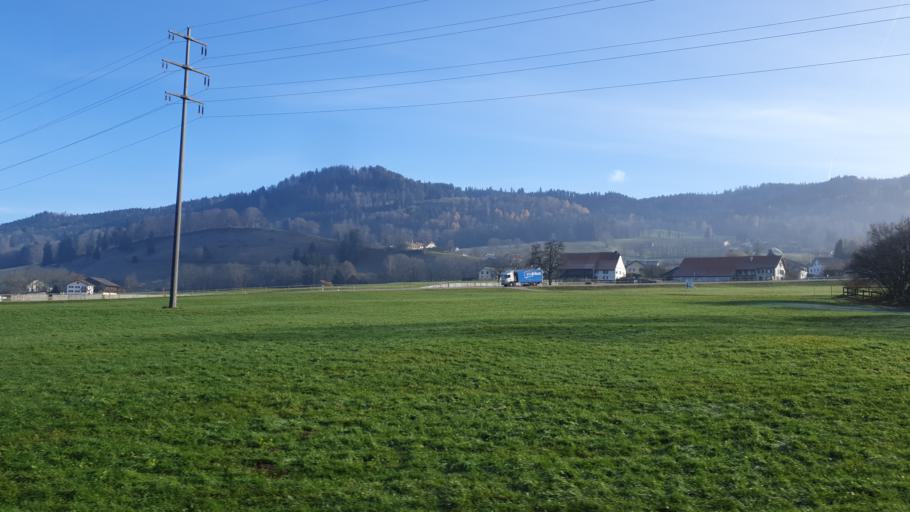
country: CH
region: Fribourg
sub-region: Veveyse District
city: Chatel-Saint-Denis
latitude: 46.5775
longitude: 6.9266
